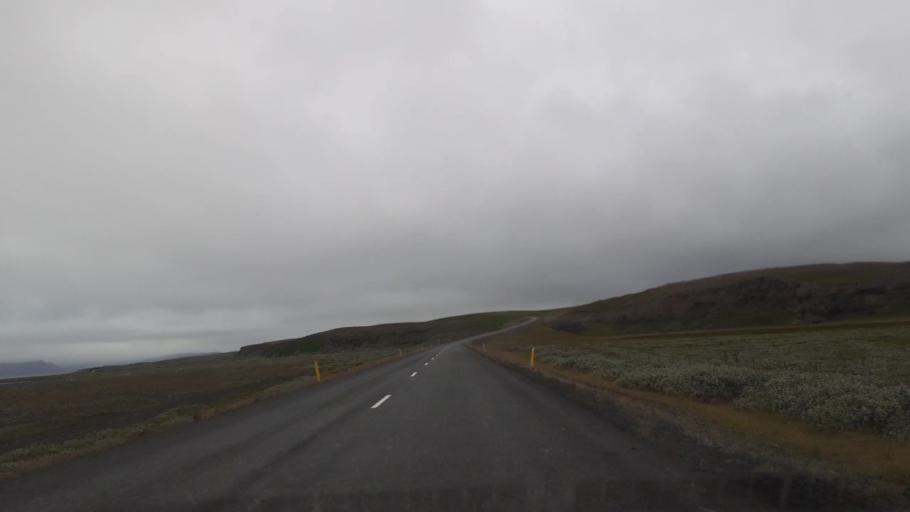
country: IS
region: Northeast
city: Husavik
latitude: 66.2037
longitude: -16.4718
